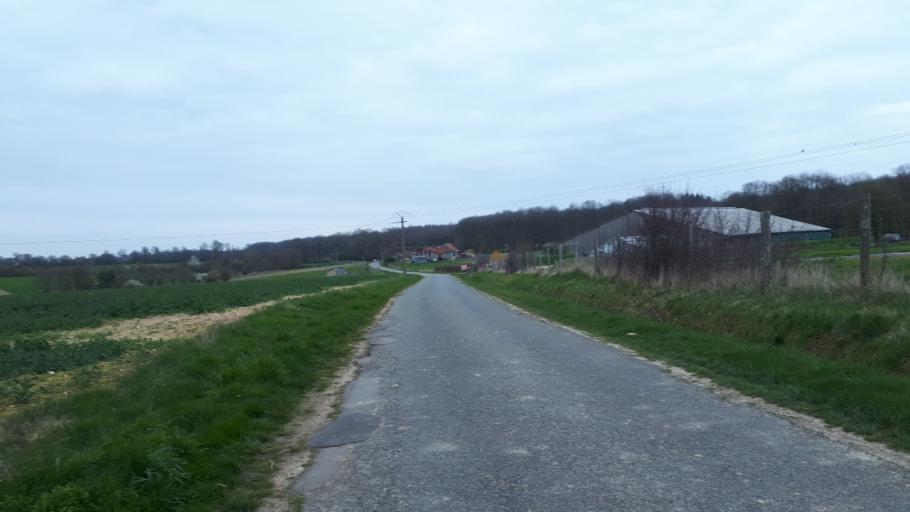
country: FR
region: Centre
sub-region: Departement du Loir-et-Cher
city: Aze
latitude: 47.8368
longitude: 1.0135
